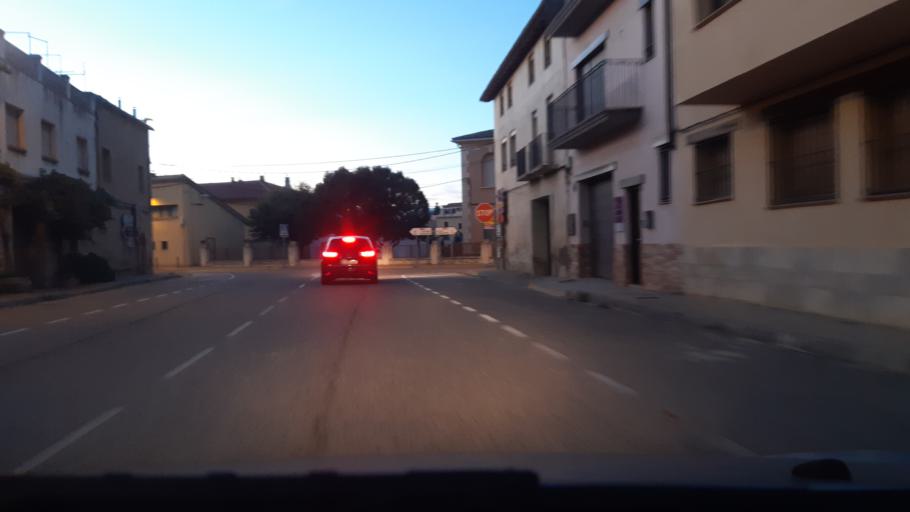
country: ES
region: Aragon
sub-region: Provincia de Teruel
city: Calaceite
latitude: 41.0137
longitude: 0.1870
